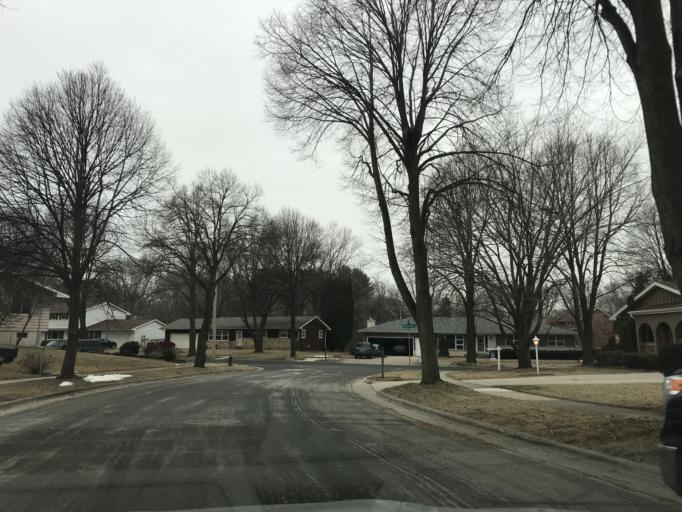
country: US
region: Wisconsin
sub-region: Dane County
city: Monona
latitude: 43.0913
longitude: -89.2906
